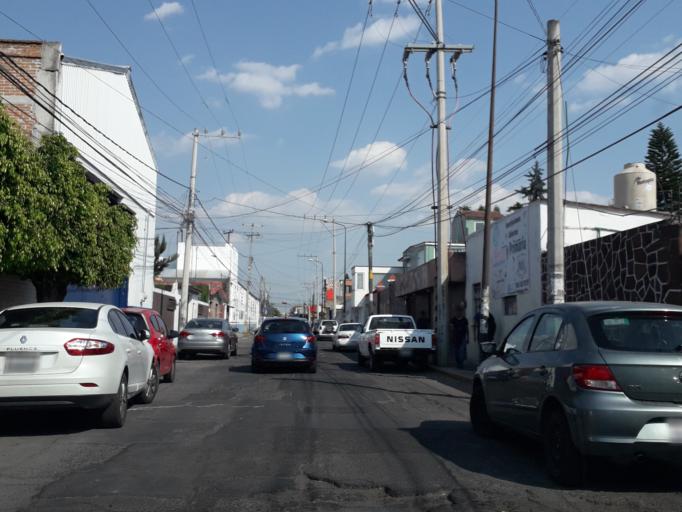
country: MX
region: Puebla
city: Puebla
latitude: 19.0170
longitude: -98.2138
